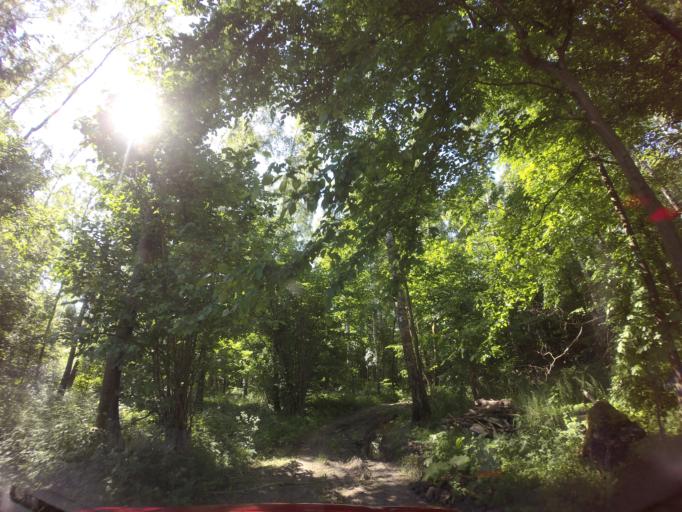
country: PL
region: West Pomeranian Voivodeship
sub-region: Powiat choszczenski
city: Choszczno
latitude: 53.1711
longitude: 15.3533
